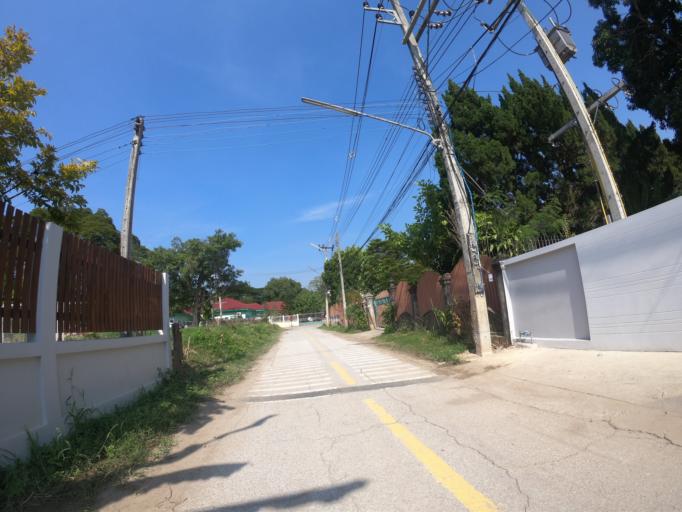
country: TH
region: Chiang Mai
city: Chiang Mai
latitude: 18.7723
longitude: 99.0042
